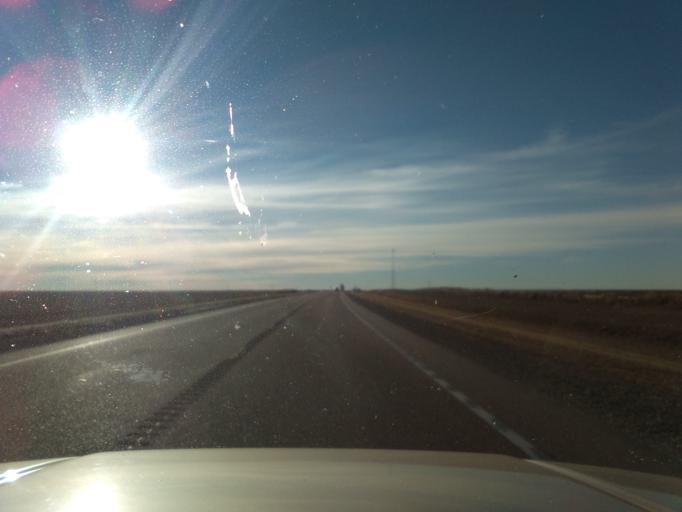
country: US
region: Kansas
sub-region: Sheridan County
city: Hoxie
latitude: 39.4847
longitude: -100.7049
